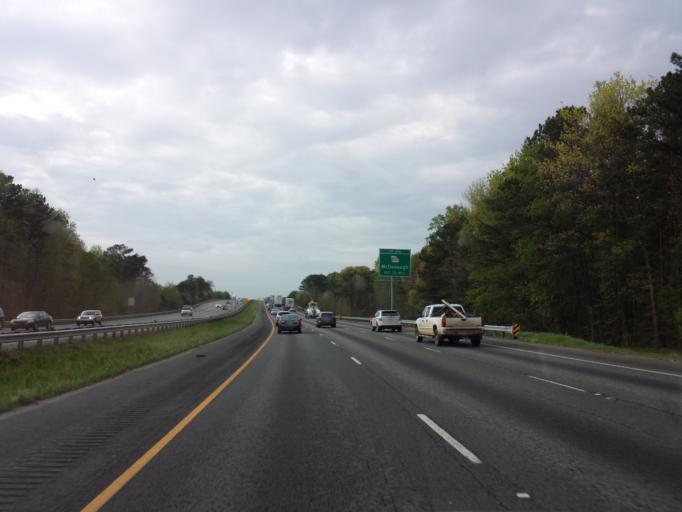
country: US
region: Georgia
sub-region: Henry County
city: McDonough
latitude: 33.4073
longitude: -84.1561
